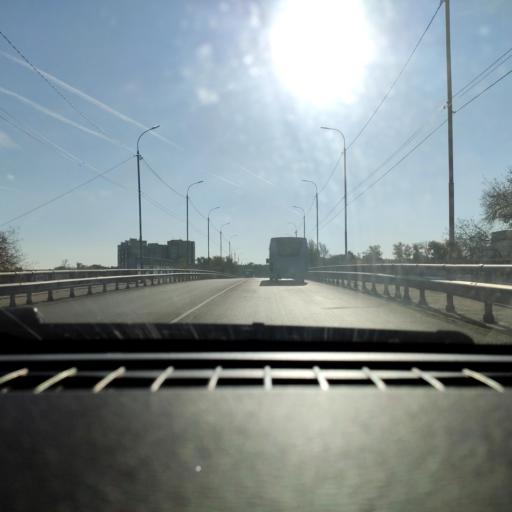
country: RU
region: Voronezj
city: Voronezh
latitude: 51.7268
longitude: 39.2607
